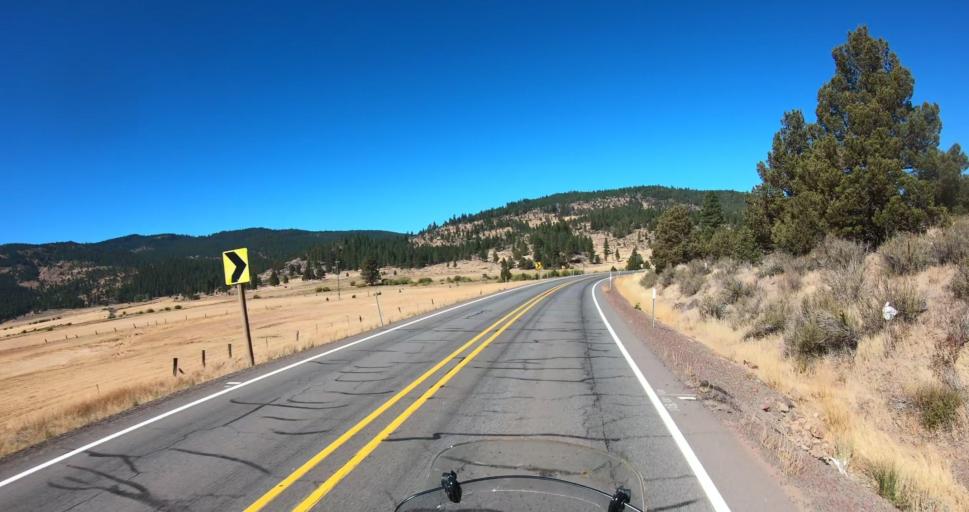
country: US
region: Oregon
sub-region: Lake County
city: Lakeview
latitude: 42.3825
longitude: -120.3062
